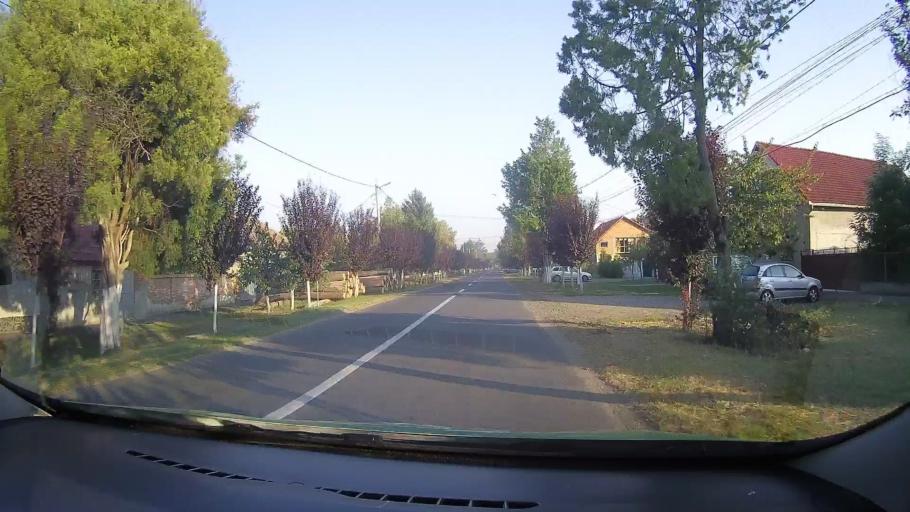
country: RO
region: Arad
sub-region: Comuna Curtici
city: Curtici
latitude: 46.3351
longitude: 21.3088
